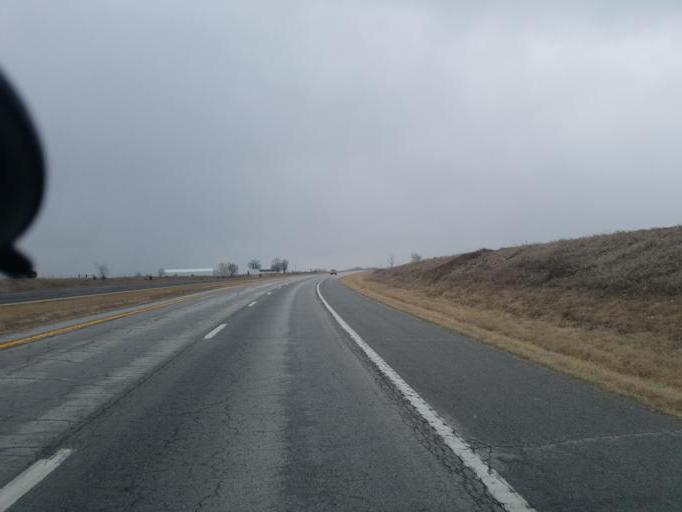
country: US
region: Missouri
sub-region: Macon County
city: La Plata
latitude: 39.8879
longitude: -92.4712
